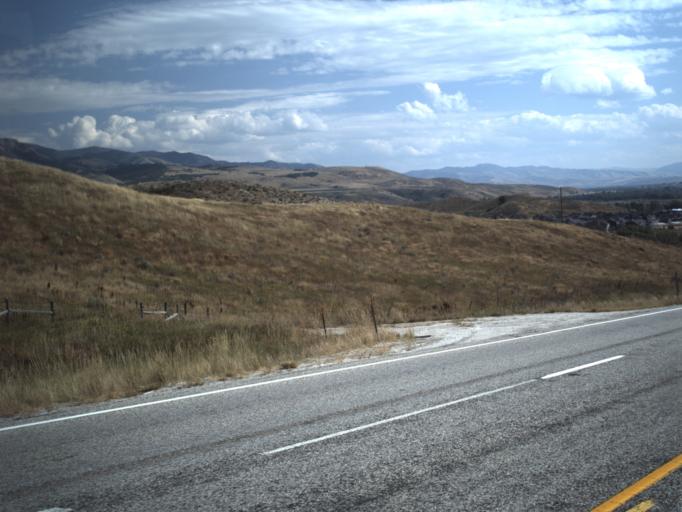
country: US
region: Utah
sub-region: Morgan County
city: Mountain Green
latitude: 41.1533
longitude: -111.7965
